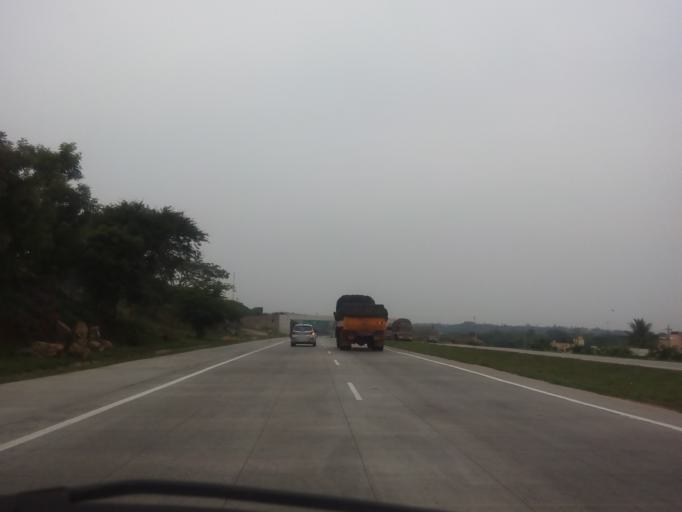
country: IN
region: Karnataka
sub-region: Bangalore Urban
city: Bangalore
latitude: 12.8845
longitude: 77.4889
